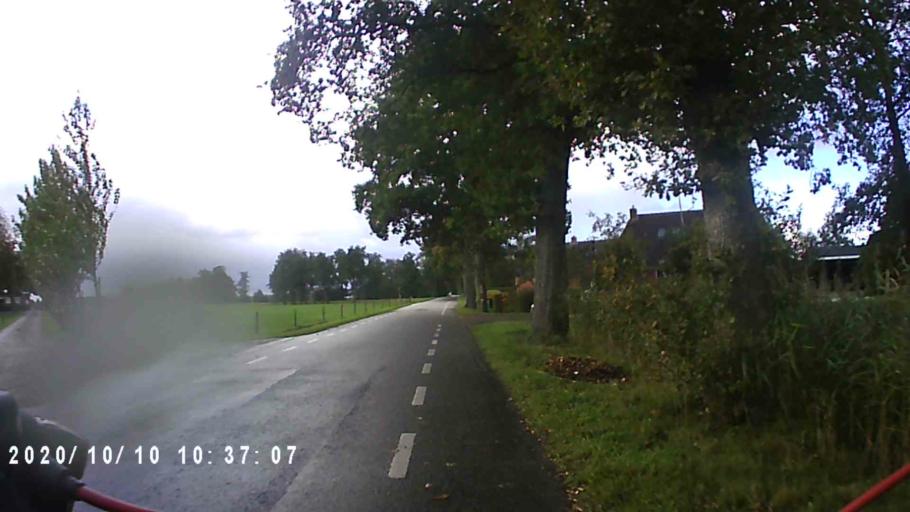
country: NL
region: Groningen
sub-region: Gemeente Grootegast
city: Grootegast
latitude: 53.1849
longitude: 6.3010
